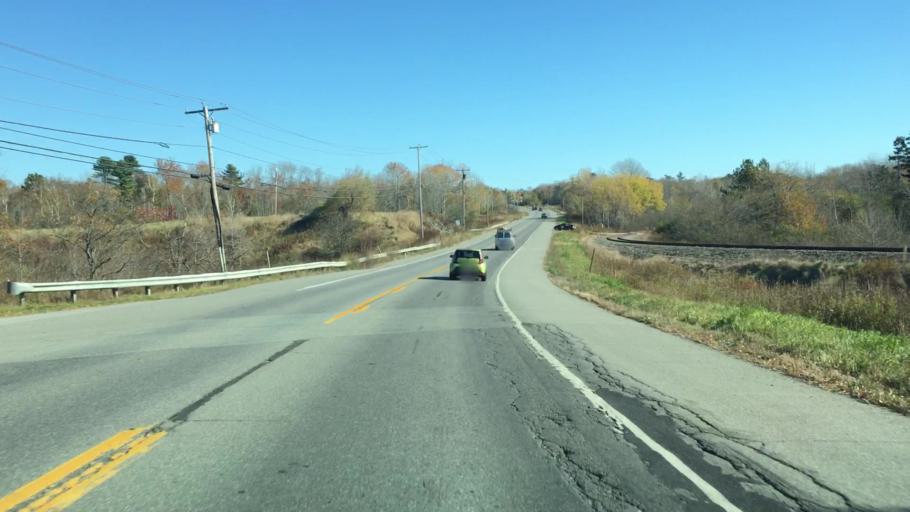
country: US
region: Maine
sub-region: Waldo County
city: Stockton Springs
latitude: 44.4691
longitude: -68.8984
